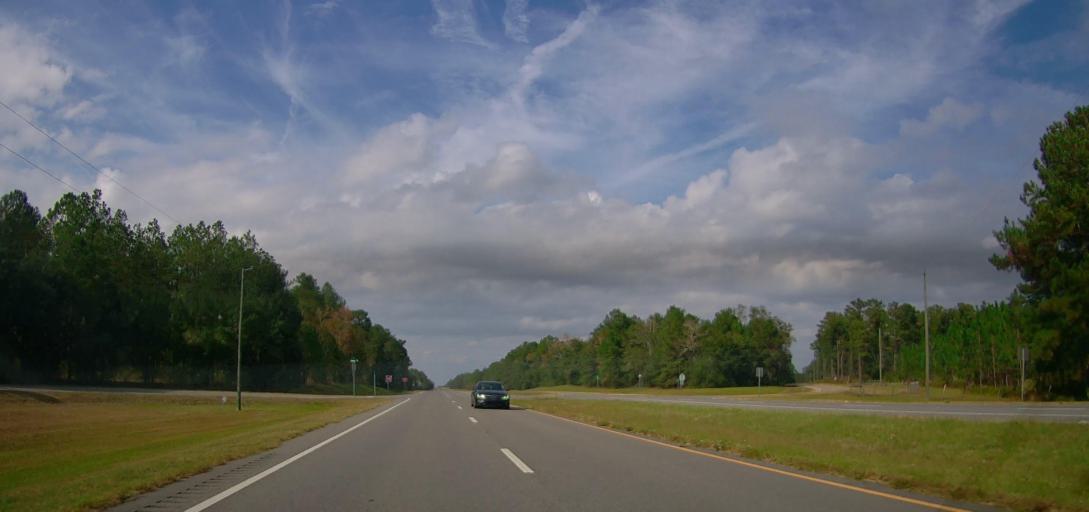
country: US
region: Georgia
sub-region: Thomas County
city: Meigs
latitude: 30.9938
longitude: -84.0450
